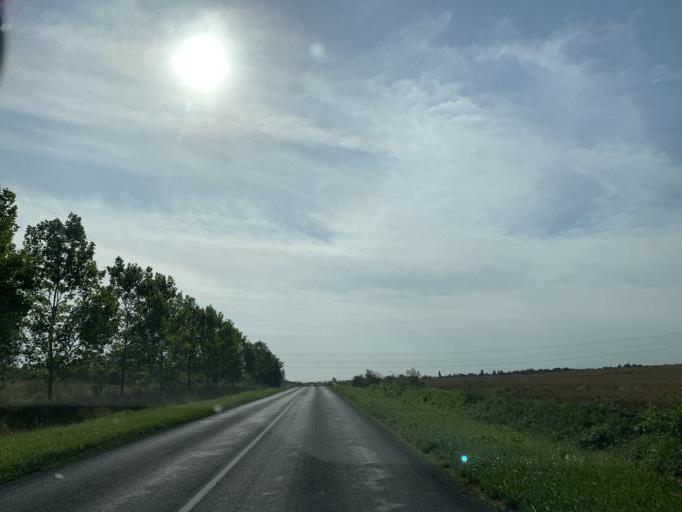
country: FR
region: Ile-de-France
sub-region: Departement de Seine-et-Marne
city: Claye-Souilly
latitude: 48.9387
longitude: 2.7000
